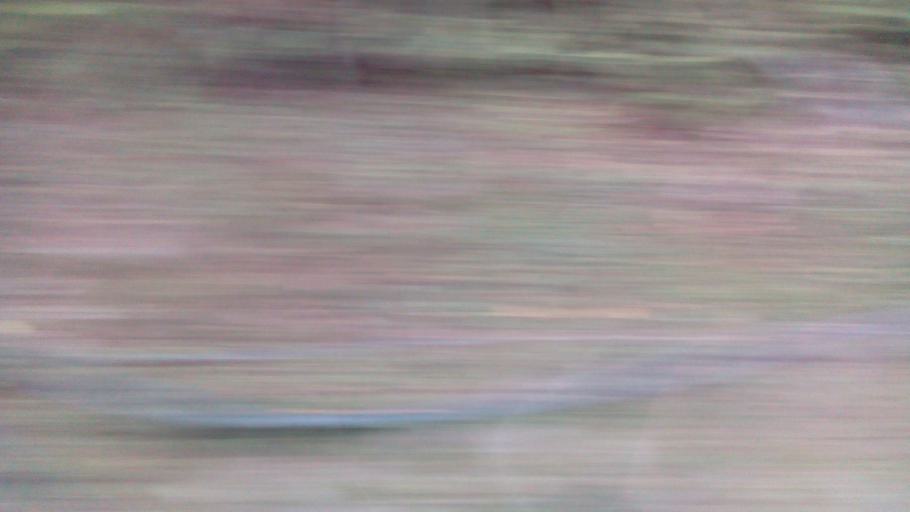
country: TW
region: Taiwan
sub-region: Yilan
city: Yilan
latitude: 24.5544
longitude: 121.4682
